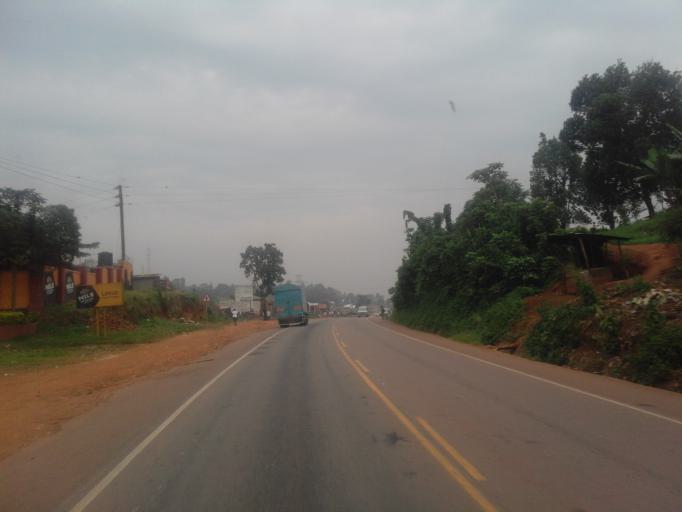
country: UG
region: Central Region
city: Lugazi
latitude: 0.3855
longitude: 32.8628
